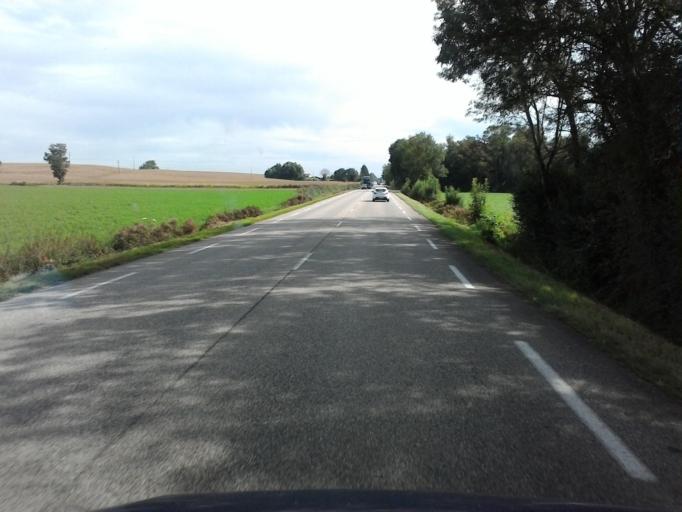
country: FR
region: Rhone-Alpes
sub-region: Departement de l'Ain
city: Saint-Cyr-sur-Menthon
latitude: 46.2708
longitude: 4.9929
